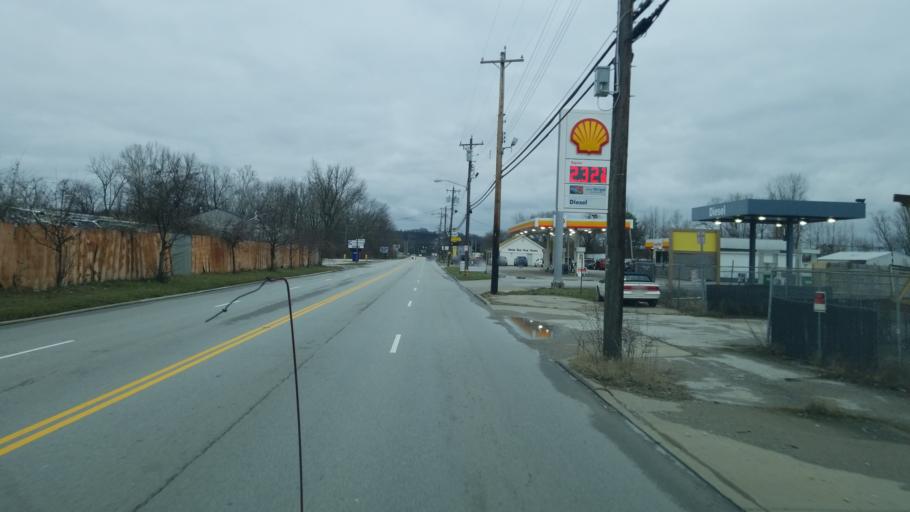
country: US
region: Kentucky
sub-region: Campbell County
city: Fort Thomas
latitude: 39.0969
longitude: -84.4301
